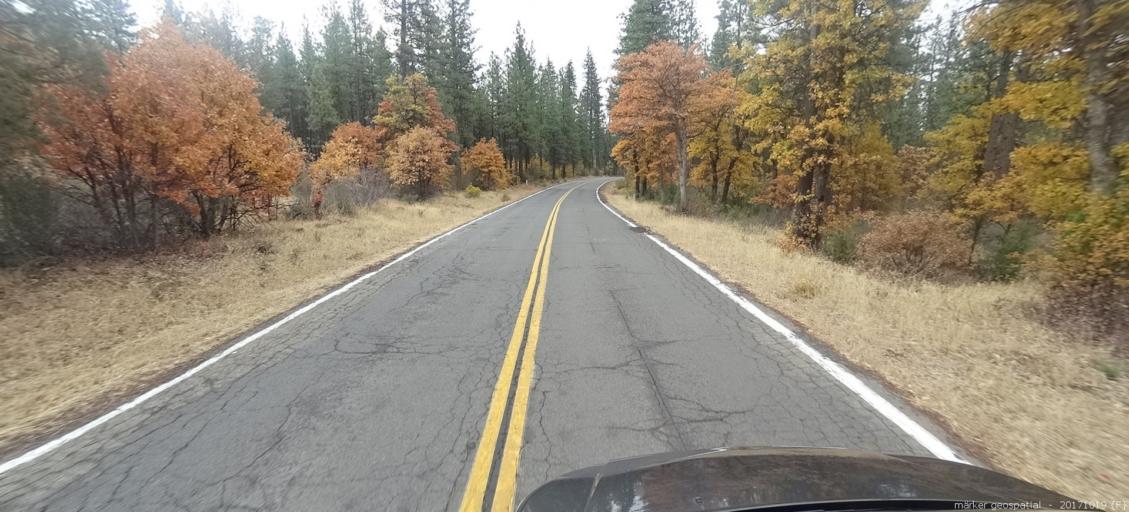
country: US
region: California
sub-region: Shasta County
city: Burney
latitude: 41.1848
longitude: -121.3630
